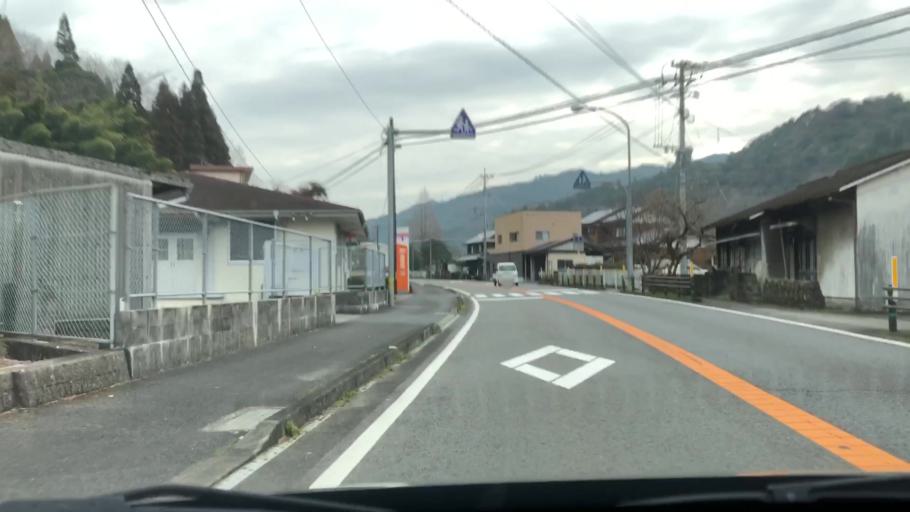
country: JP
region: Oita
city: Usuki
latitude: 33.0067
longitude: 131.7161
